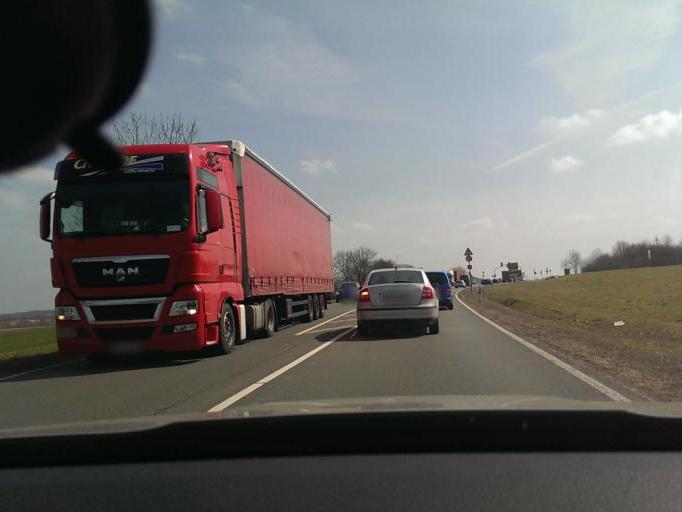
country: DE
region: Thuringia
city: Hohenkirchen
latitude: 50.8403
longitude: 10.7189
